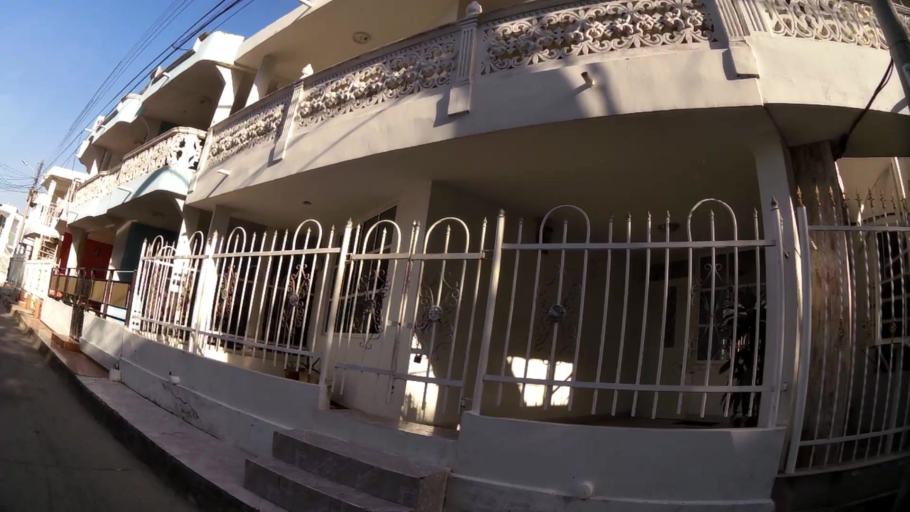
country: CO
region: Bolivar
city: Cartagena
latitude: 10.3829
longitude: -75.4820
